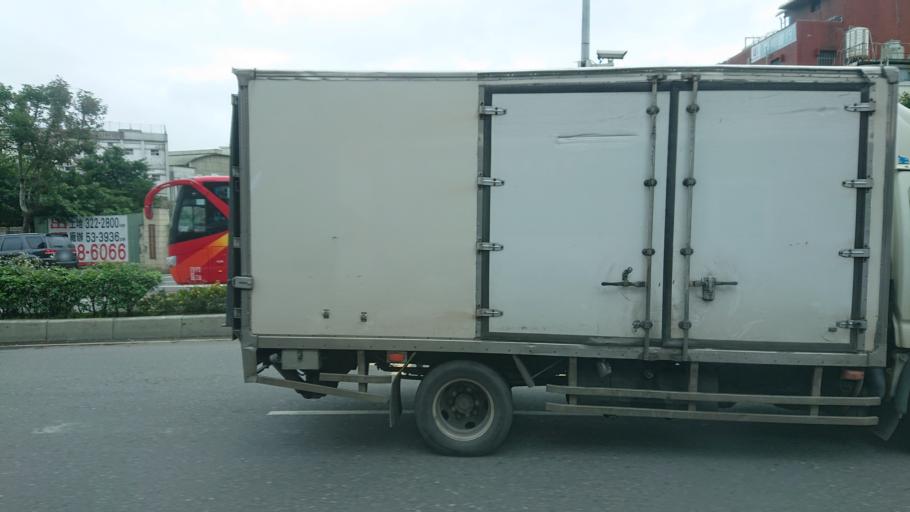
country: TW
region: Taipei
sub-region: Taipei
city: Banqiao
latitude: 24.9667
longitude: 121.4360
